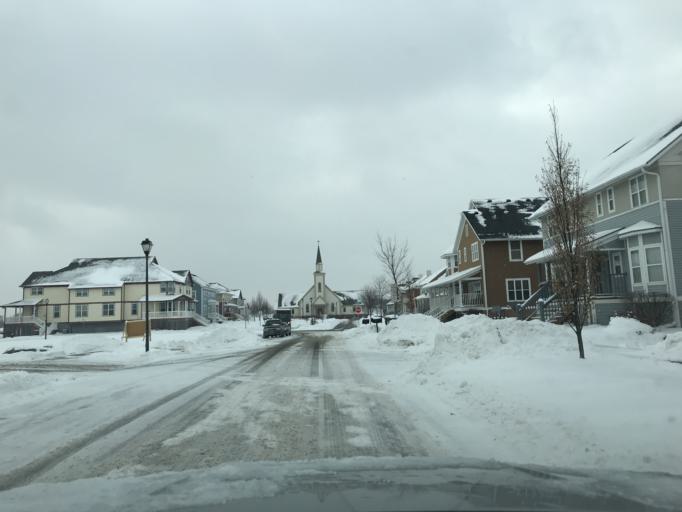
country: US
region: Wisconsin
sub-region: Dane County
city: Sun Prairie
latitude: 43.1677
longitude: -89.2766
